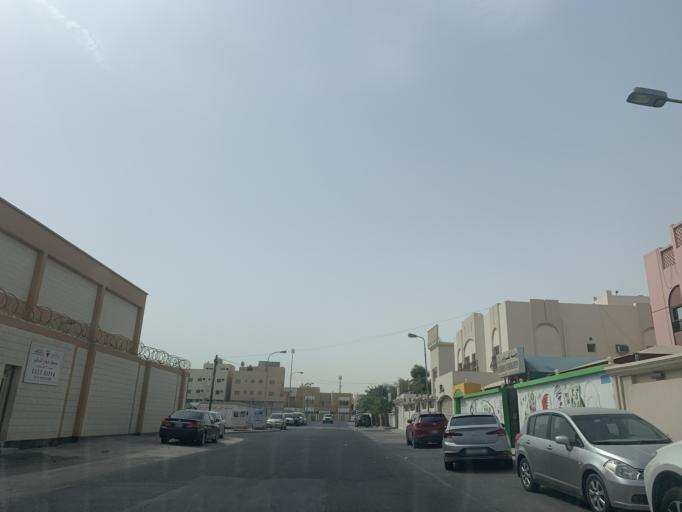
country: BH
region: Northern
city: Ar Rifa'
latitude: 26.1311
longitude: 50.5696
